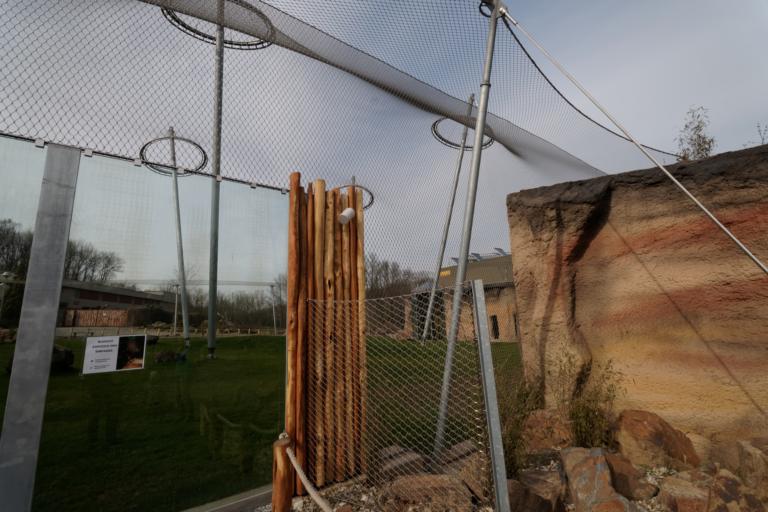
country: CZ
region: Moravskoslezsky
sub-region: Okres Ostrava-Mesto
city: Ostrava
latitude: 49.8497
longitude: 18.3274
